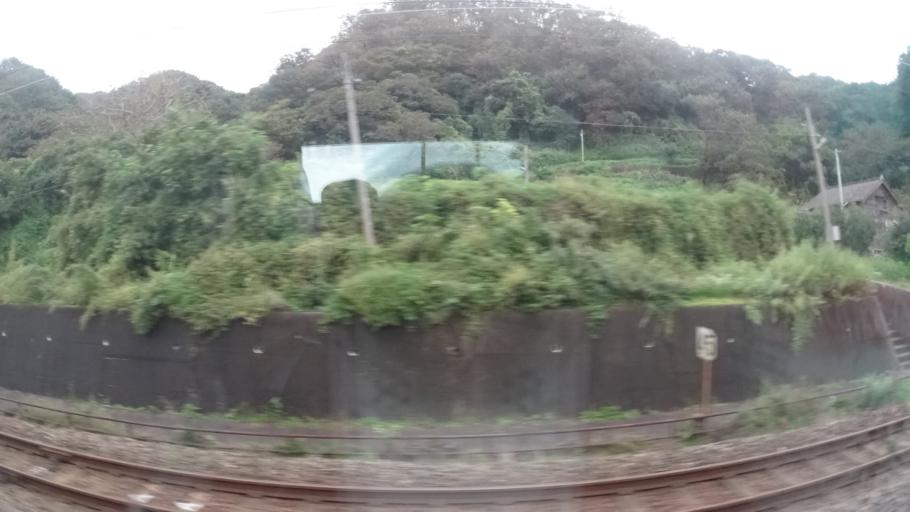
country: JP
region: Yamagata
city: Tsuruoka
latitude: 38.6274
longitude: 139.5899
